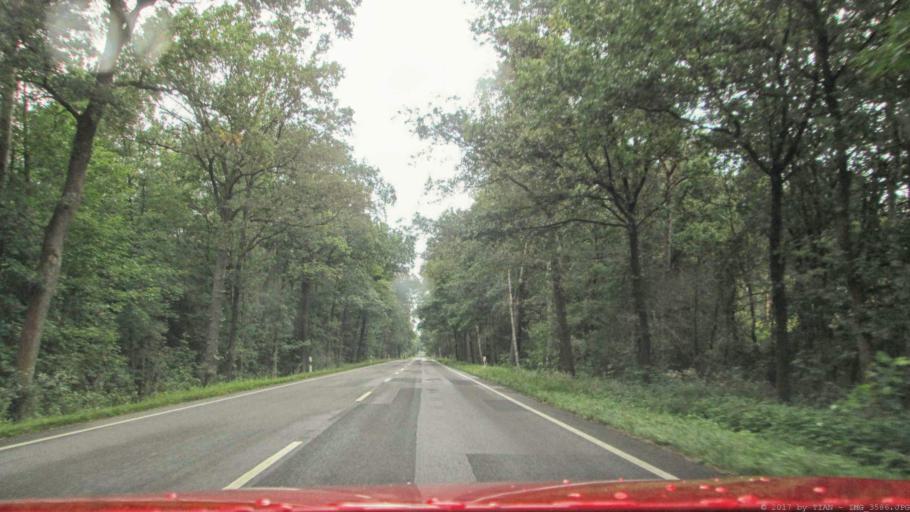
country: DE
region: Lower Saxony
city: Dedelstorf
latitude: 52.6914
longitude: 10.4741
